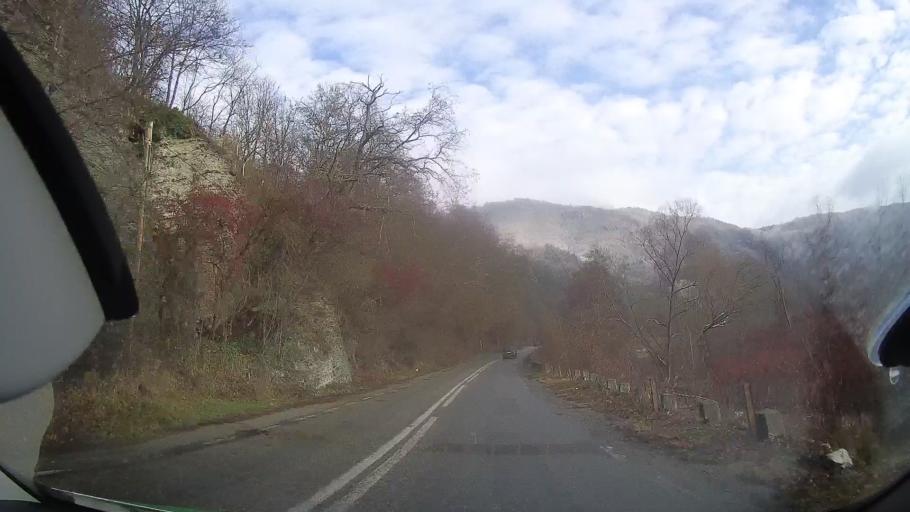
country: RO
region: Alba
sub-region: Comuna Lupsa
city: Lupsa
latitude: 46.3840
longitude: 23.2305
